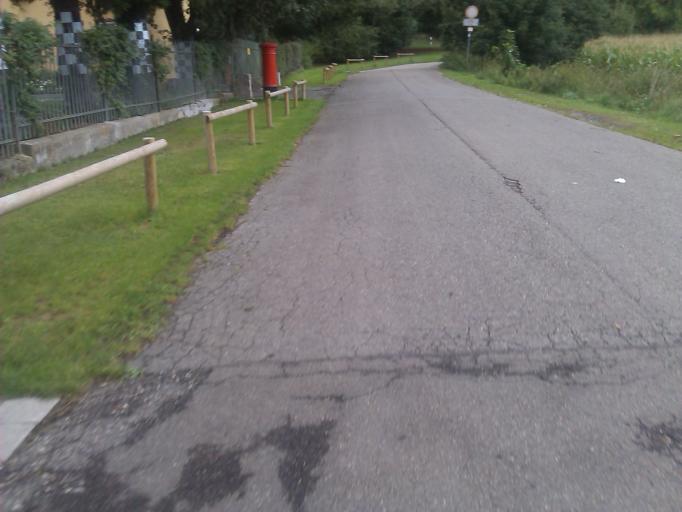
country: DE
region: Baden-Wuerttemberg
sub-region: Tuebingen Region
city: Pliezhausen
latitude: 48.5672
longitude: 9.2237
